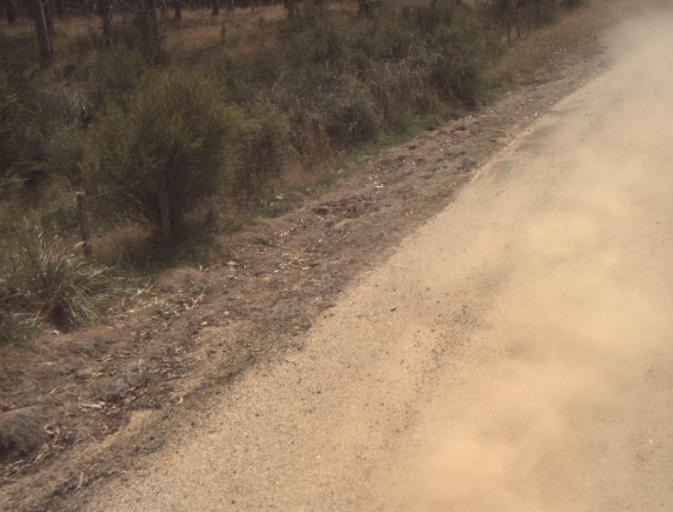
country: AU
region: Tasmania
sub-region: Dorset
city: Scottsdale
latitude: -41.4116
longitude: 147.5263
